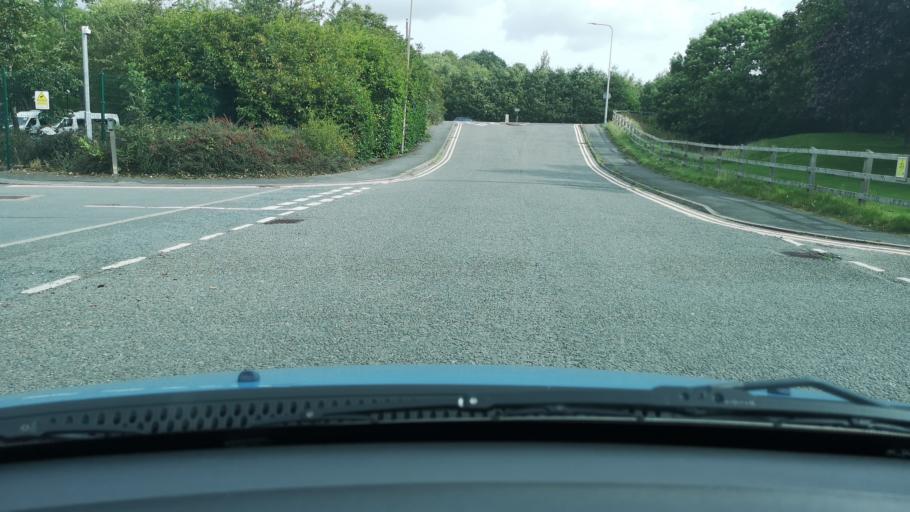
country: GB
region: England
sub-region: North Lincolnshire
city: Scunthorpe
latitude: 53.5805
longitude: -0.6701
